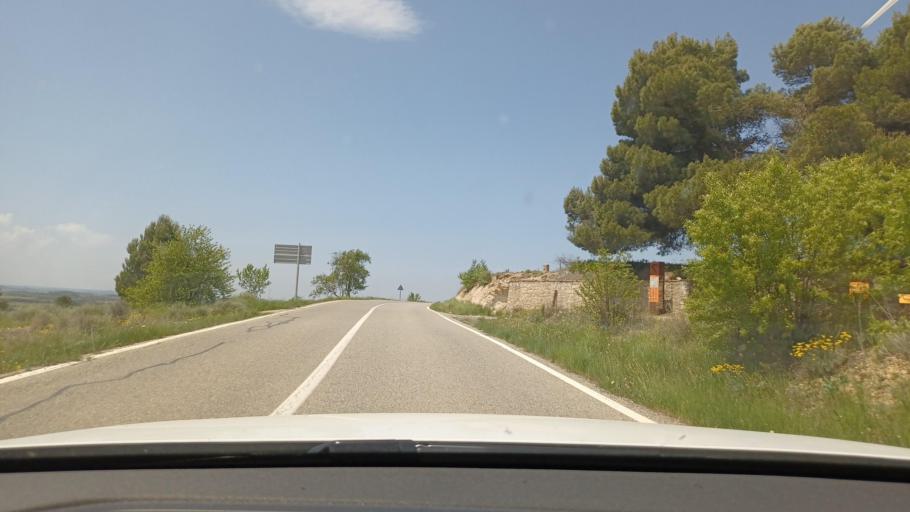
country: ES
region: Catalonia
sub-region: Provincia de Tarragona
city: Vilalba dels Arcs
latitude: 41.1094
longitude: 0.4194
